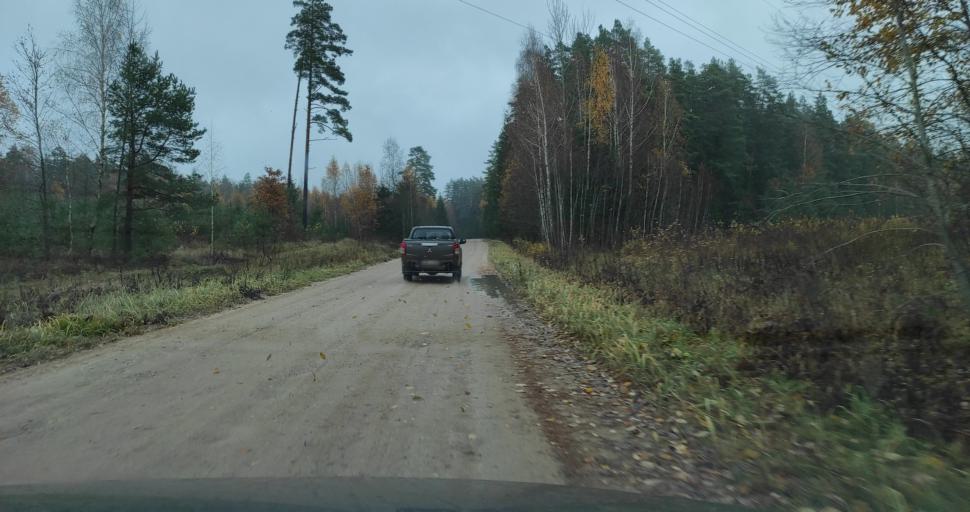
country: LV
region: Skrunda
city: Skrunda
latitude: 56.6843
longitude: 22.0696
